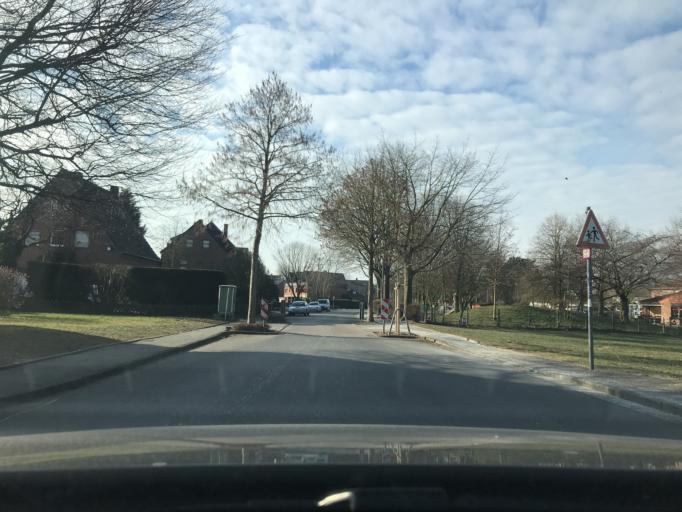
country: DE
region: North Rhine-Westphalia
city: Tonisvorst
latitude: 51.3264
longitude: 6.4985
